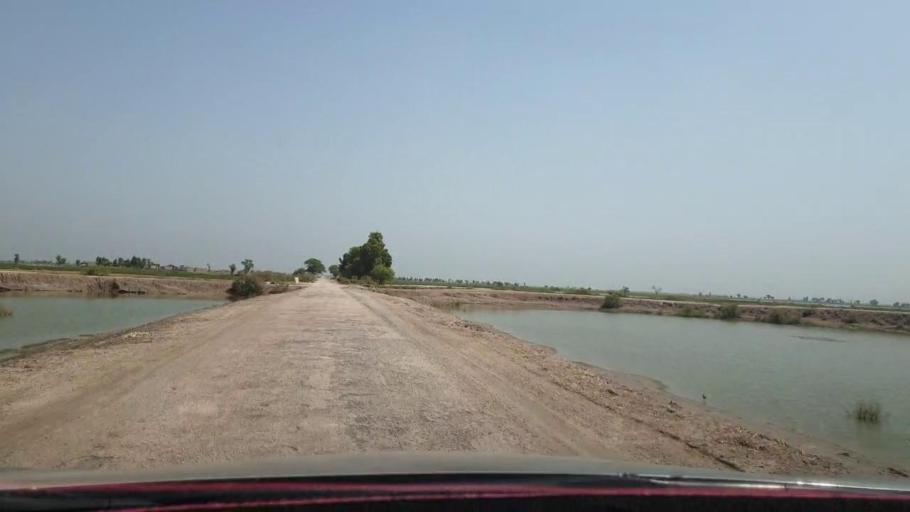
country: PK
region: Sindh
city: Warah
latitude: 27.3826
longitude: 67.7846
